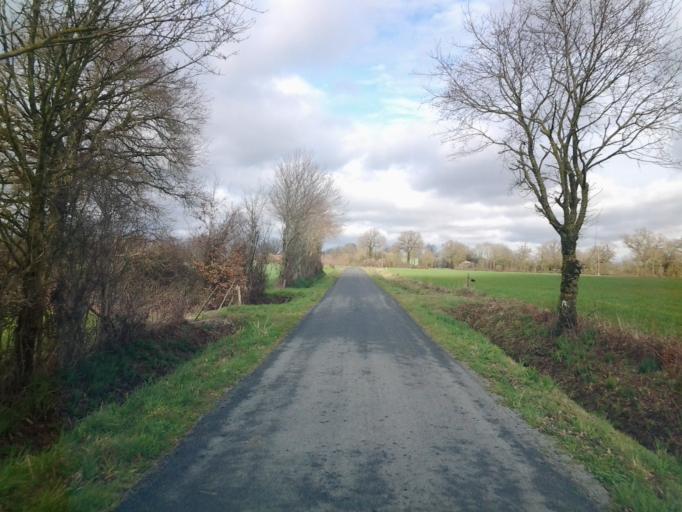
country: FR
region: Pays de la Loire
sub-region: Departement de la Vendee
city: La Chaize-le-Vicomte
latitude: 46.6551
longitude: -1.3551
